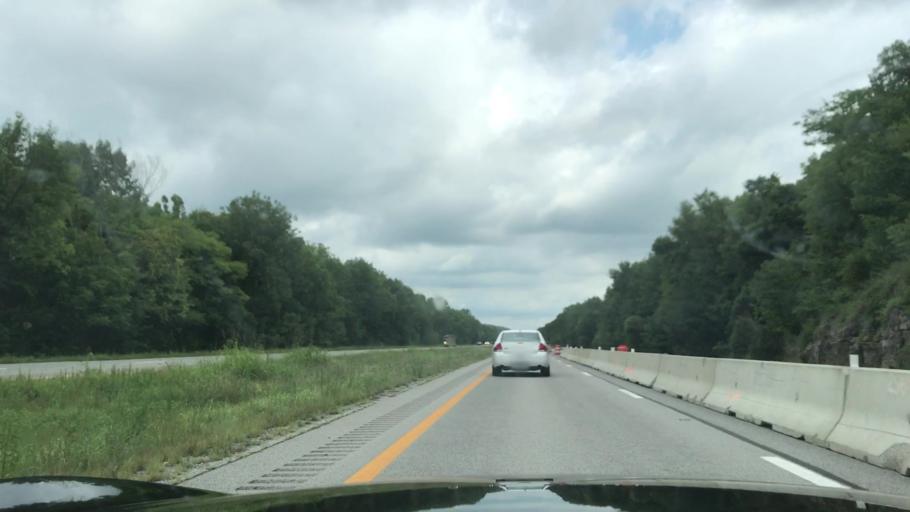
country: US
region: Kentucky
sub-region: Butler County
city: Morgantown
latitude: 37.1262
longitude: -86.6446
